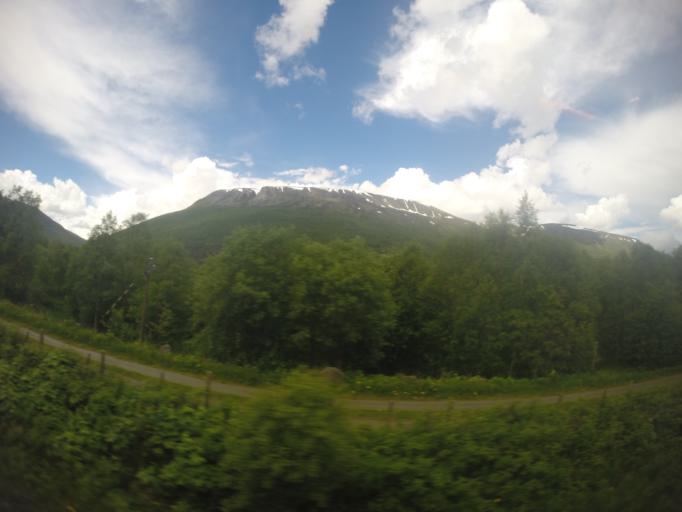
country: NO
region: Sor-Trondelag
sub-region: Oppdal
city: Oppdal
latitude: 62.5063
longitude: 9.5972
